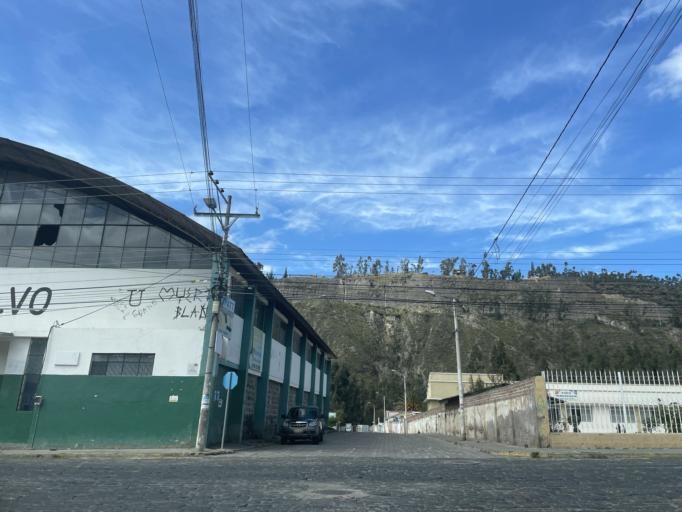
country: EC
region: Chimborazo
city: Guano
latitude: -1.6080
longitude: -78.6429
